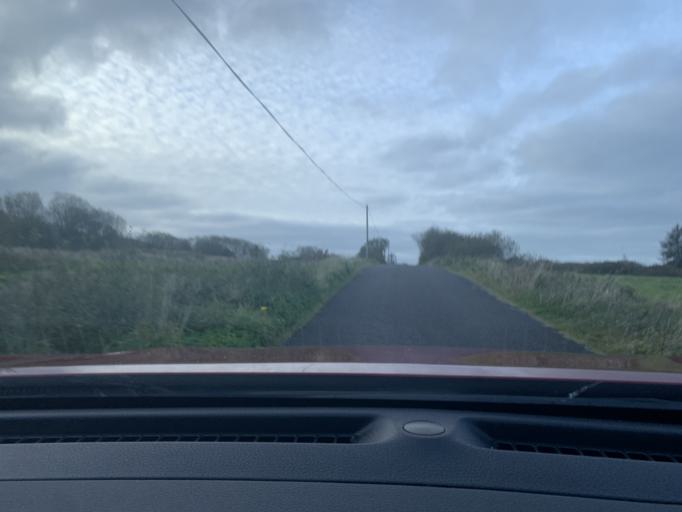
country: IE
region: Connaught
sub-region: Roscommon
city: Ballaghaderreen
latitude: 53.9367
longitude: -8.5915
